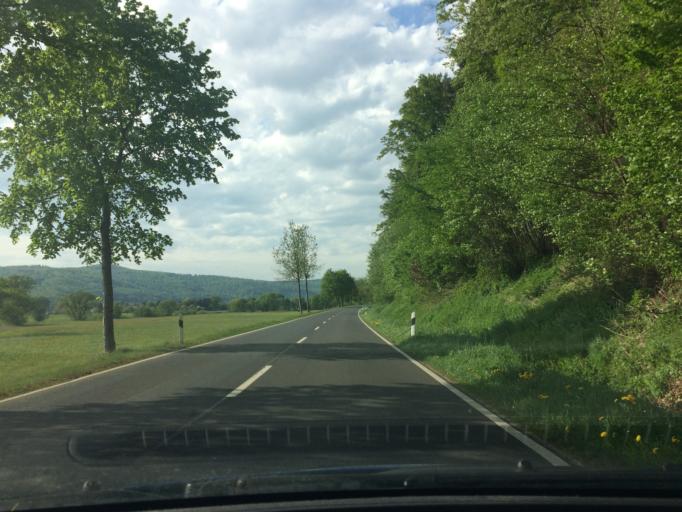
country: DE
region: Lower Saxony
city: Buhren
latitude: 51.4839
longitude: 9.6193
